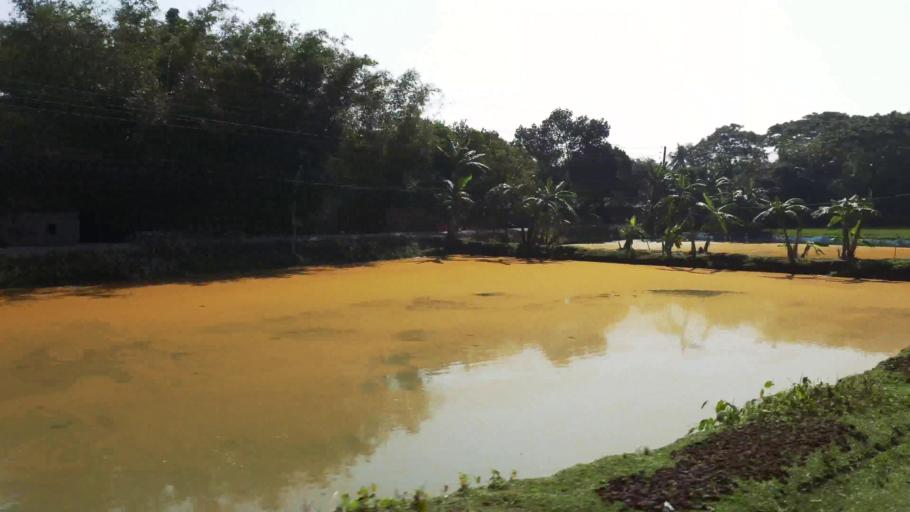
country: BD
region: Dhaka
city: Gafargaon
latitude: 24.5535
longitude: 90.5084
